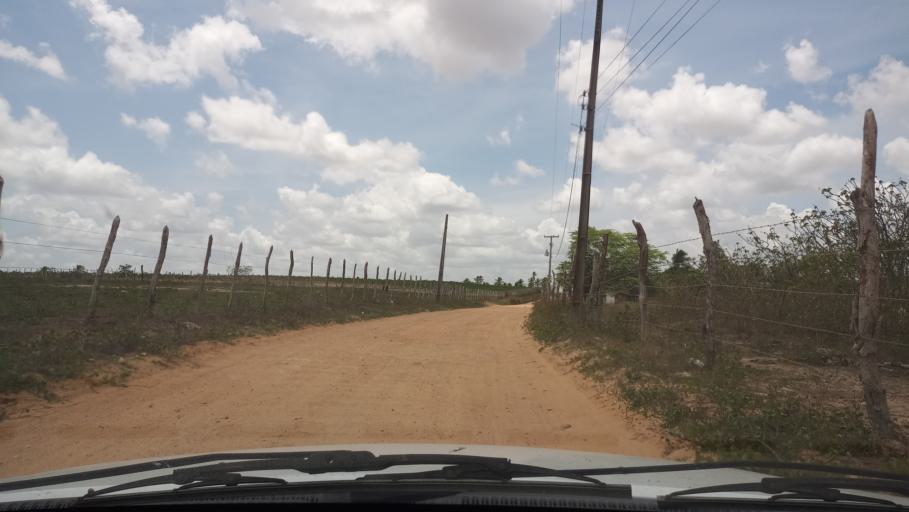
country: BR
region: Rio Grande do Norte
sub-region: Brejinho
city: Brejinho
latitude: -6.3036
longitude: -35.3454
